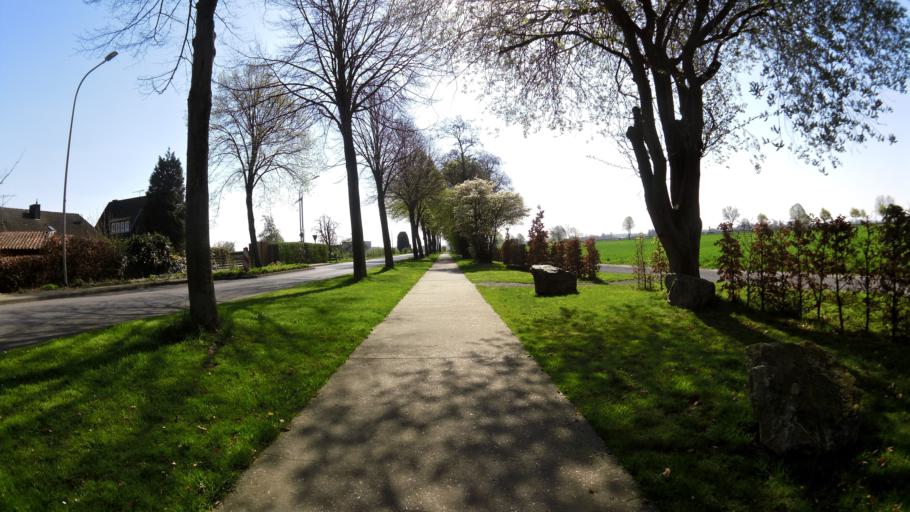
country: DE
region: North Rhine-Westphalia
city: Baesweiler
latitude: 50.9499
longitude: 6.1761
